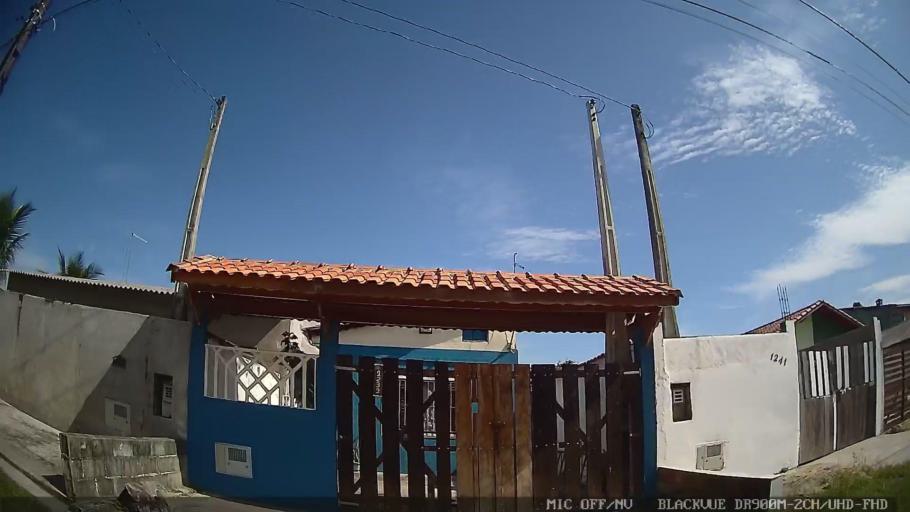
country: BR
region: Sao Paulo
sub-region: Itanhaem
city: Itanhaem
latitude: -24.1492
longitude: -46.7419
